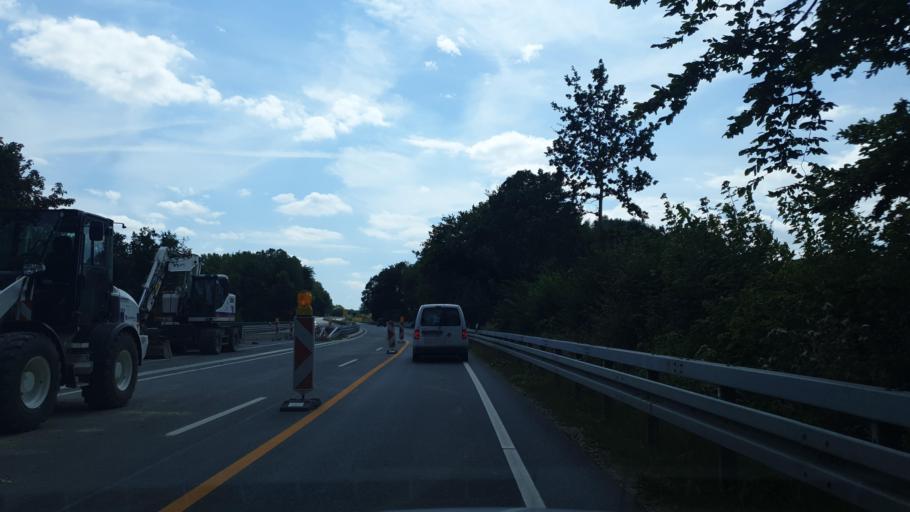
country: DE
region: North Rhine-Westphalia
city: Loehne
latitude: 52.1828
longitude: 8.7482
